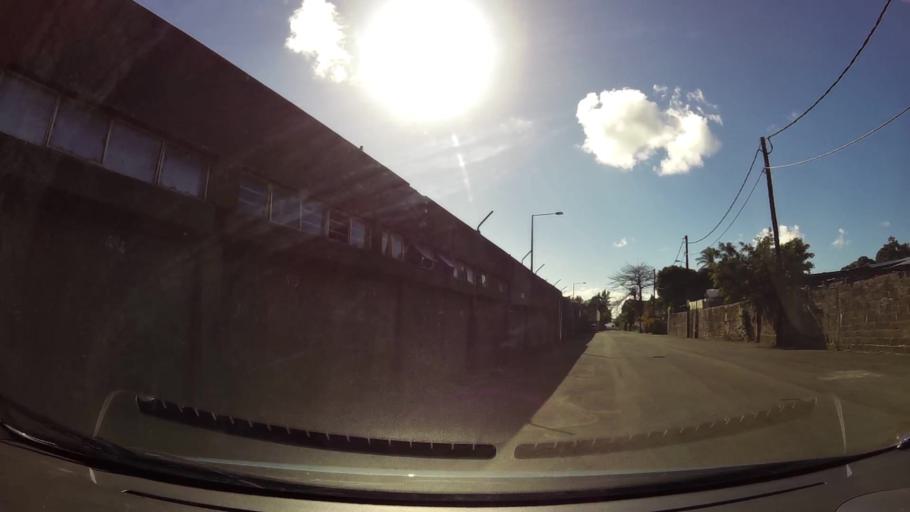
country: MU
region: Grand Port
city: Mahebourg
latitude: -20.4049
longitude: 57.7053
